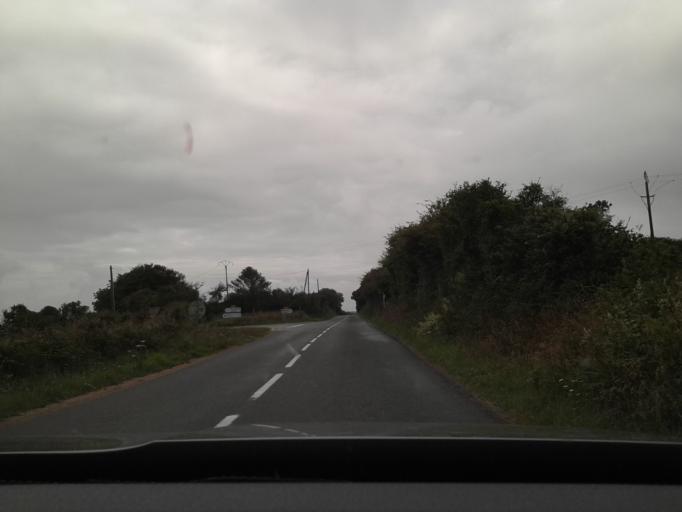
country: FR
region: Lower Normandy
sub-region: Departement de la Manche
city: Beaumont-Hague
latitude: 49.6725
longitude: -1.8103
